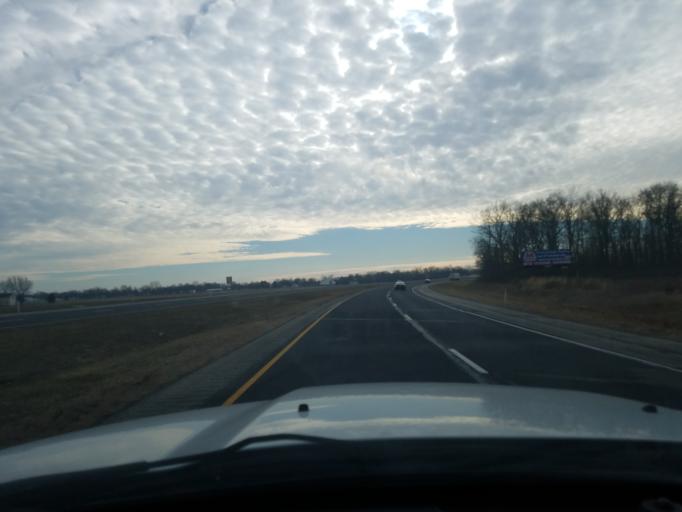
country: US
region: Indiana
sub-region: Huntington County
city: Markle
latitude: 40.8391
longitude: -85.3446
